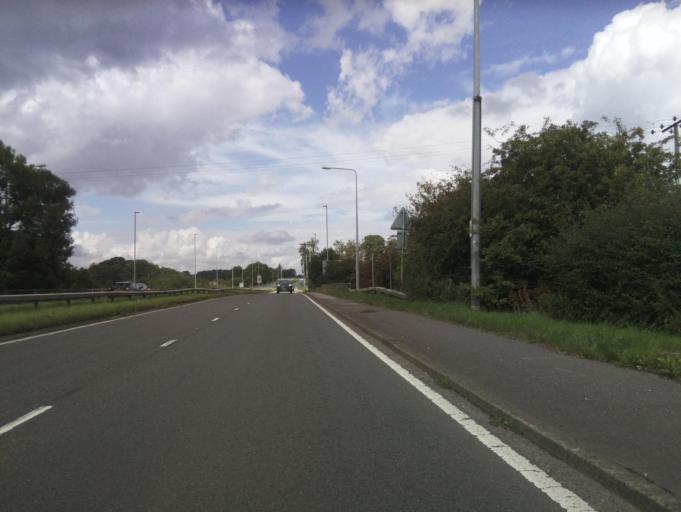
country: GB
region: England
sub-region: Staffordshire
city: Barlaston
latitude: 52.9497
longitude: -2.1908
